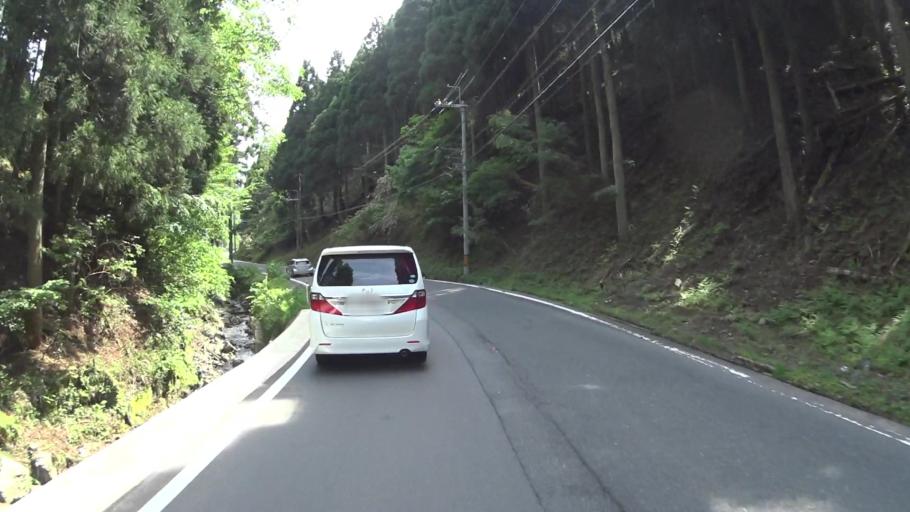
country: JP
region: Fukui
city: Obama
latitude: 35.4065
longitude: 135.9338
